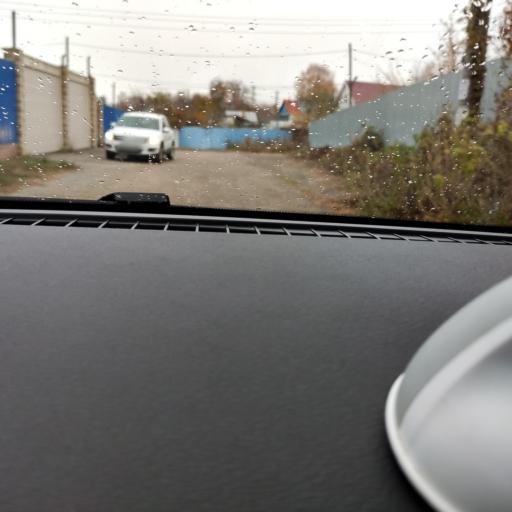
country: RU
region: Samara
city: Petra-Dubrava
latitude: 53.2982
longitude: 50.3049
